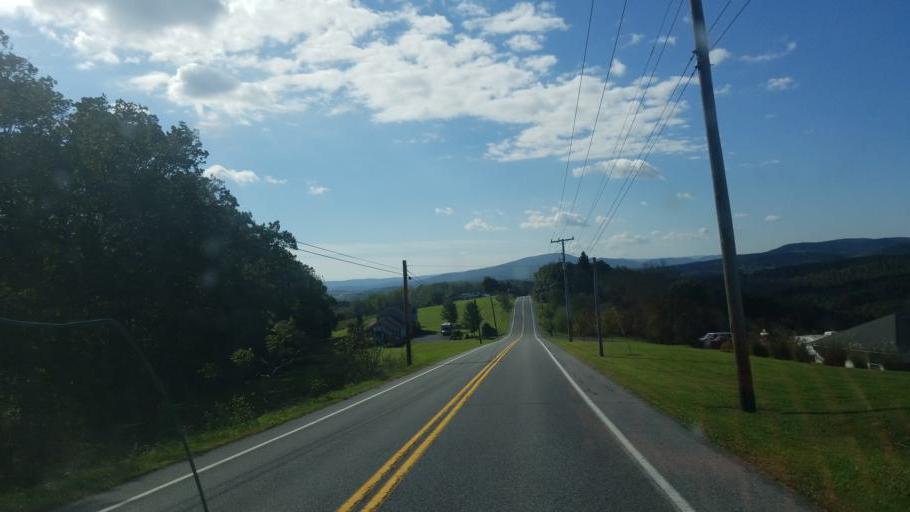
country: US
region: Pennsylvania
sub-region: Bedford County
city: Bedford
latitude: 40.1260
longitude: -78.5221
